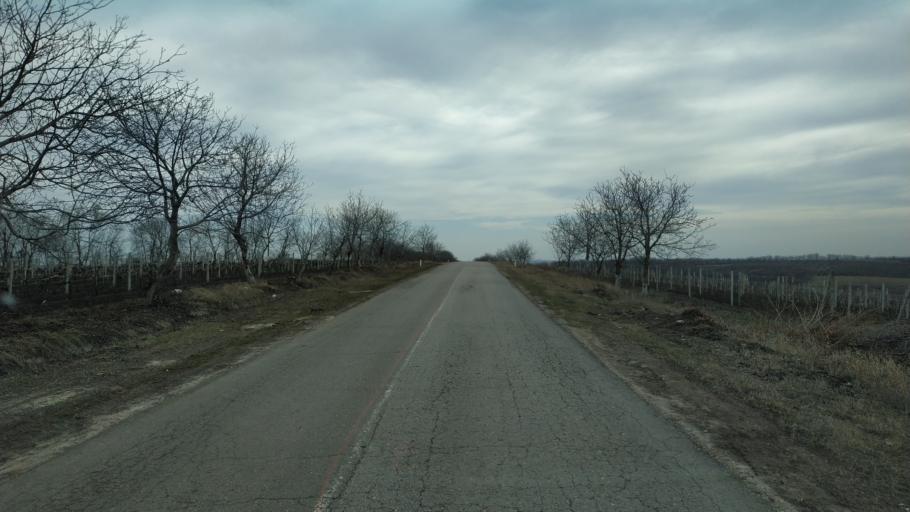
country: MD
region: Nisporeni
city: Nisporeni
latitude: 46.9520
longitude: 28.2382
